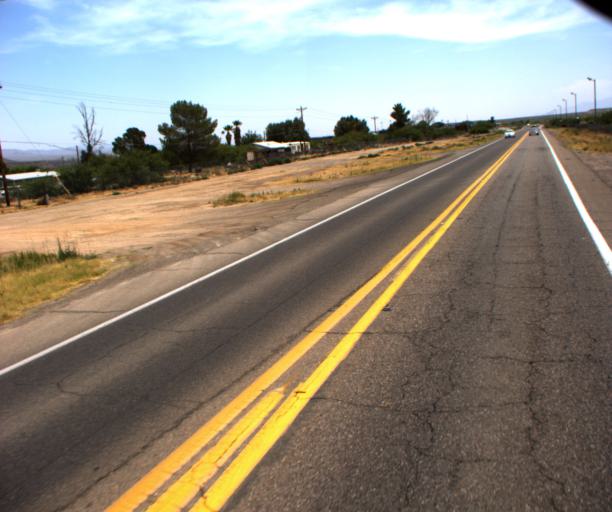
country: US
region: Arizona
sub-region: Graham County
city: Bylas
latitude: 33.1244
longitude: -110.1140
